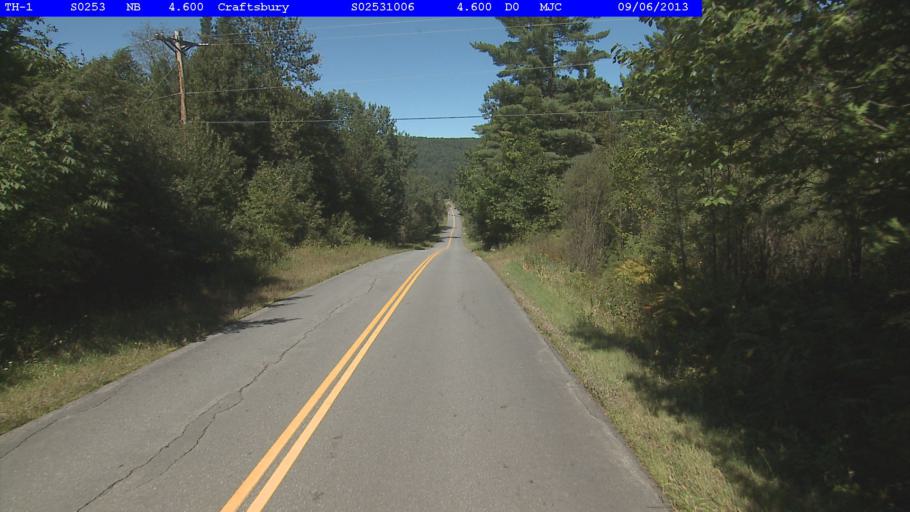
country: US
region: Vermont
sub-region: Caledonia County
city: Hardwick
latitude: 44.6715
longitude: -72.3921
